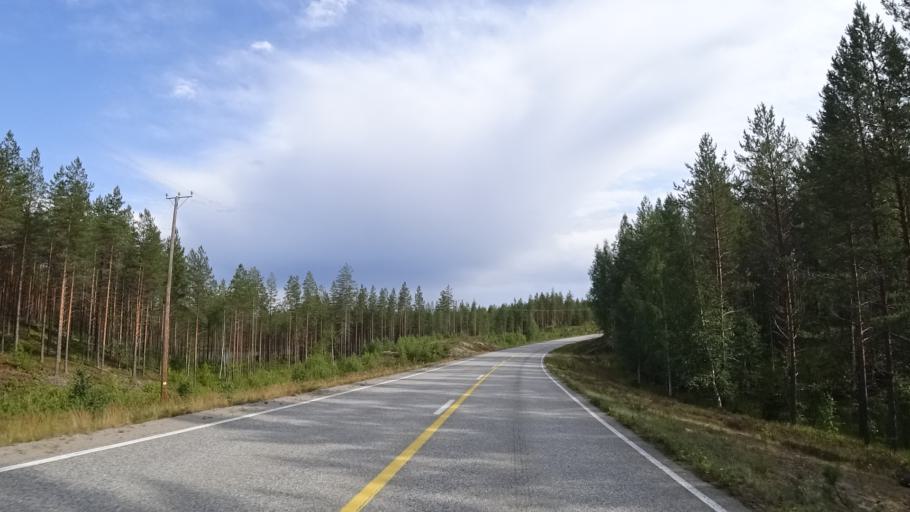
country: FI
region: North Karelia
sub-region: Joensuu
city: Ilomantsi
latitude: 62.6356
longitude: 31.0900
